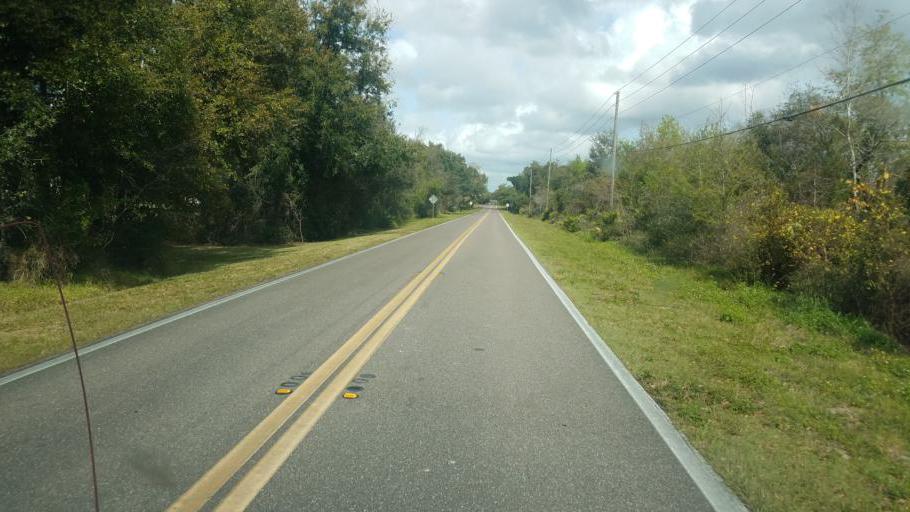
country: US
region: Florida
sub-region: Polk County
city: Dundee
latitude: 28.0589
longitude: -81.5543
